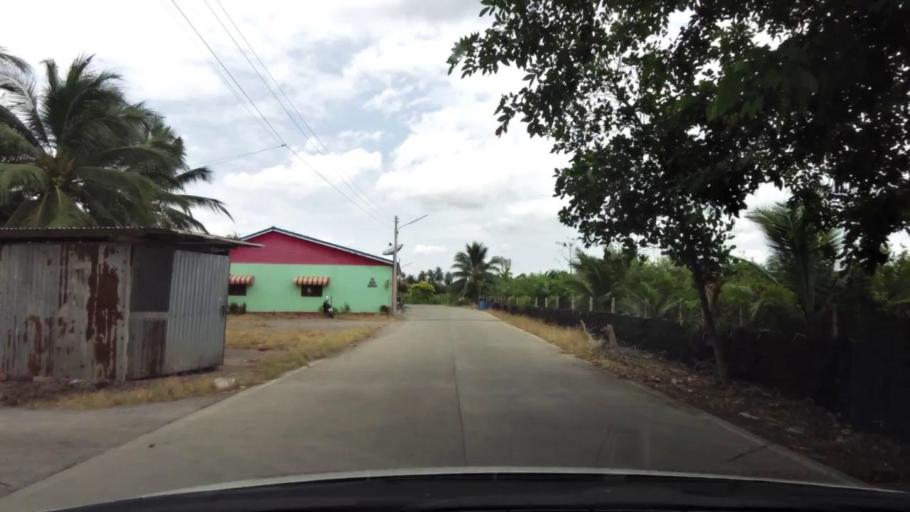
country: TH
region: Samut Sakhon
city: Ban Phaeo
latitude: 13.5673
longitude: 100.0358
